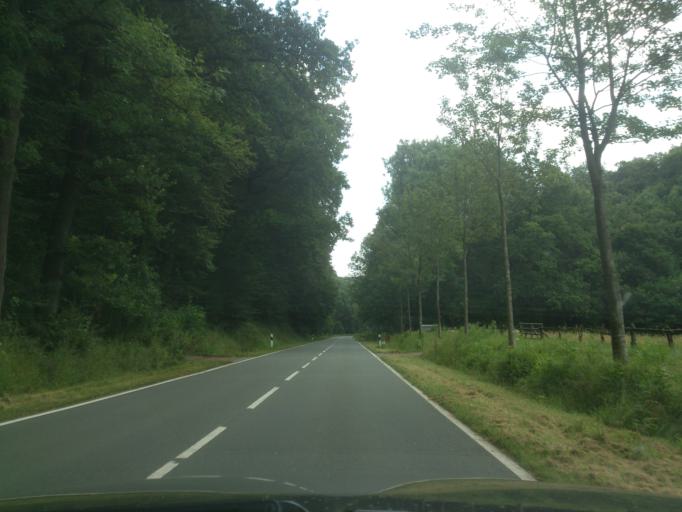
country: DE
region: North Rhine-Westphalia
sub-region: Regierungsbezirk Detmold
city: Bad Driburg
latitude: 51.7051
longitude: 9.0404
